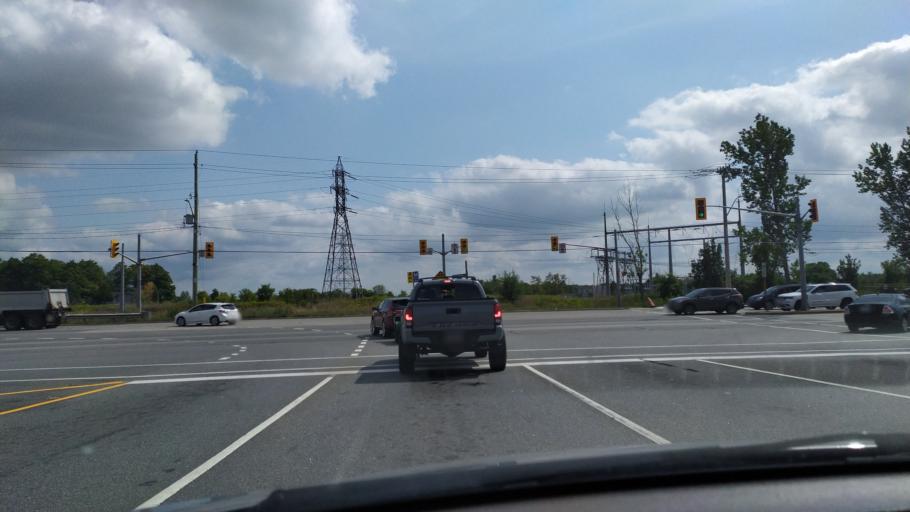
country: CA
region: Ontario
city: Kitchener
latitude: 43.4246
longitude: -80.4349
